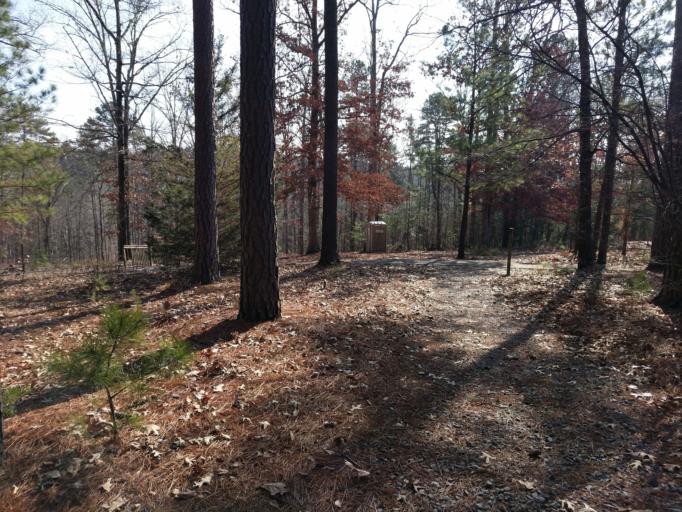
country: US
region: South Carolina
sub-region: Spartanburg County
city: Lyman
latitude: 34.9297
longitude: -82.1267
